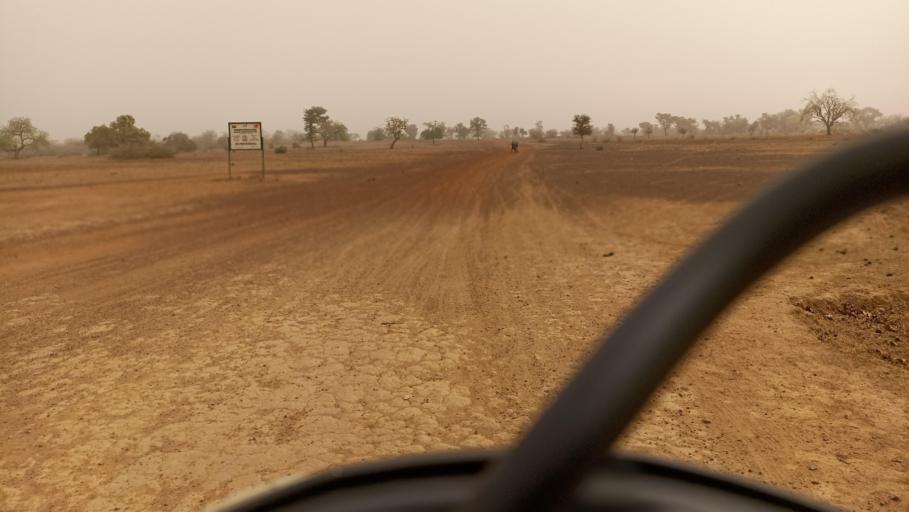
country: BF
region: Nord
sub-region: Province du Zondoma
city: Gourcy
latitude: 13.2892
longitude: -2.5248
